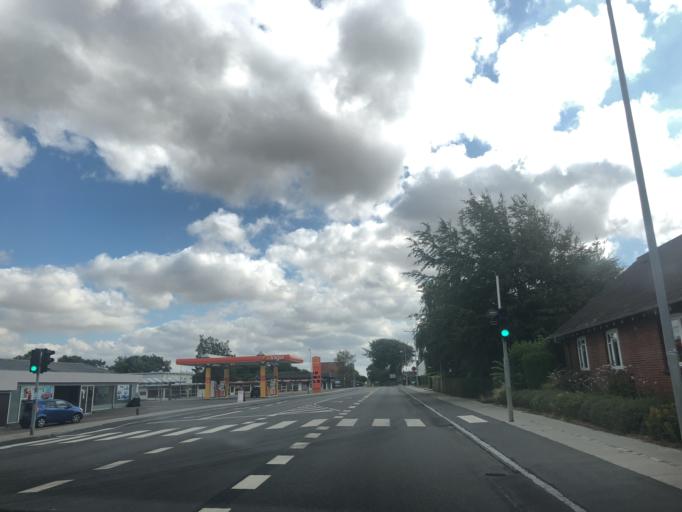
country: DK
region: Central Jutland
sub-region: Struer Kommune
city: Struer
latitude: 56.4802
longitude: 8.6049
